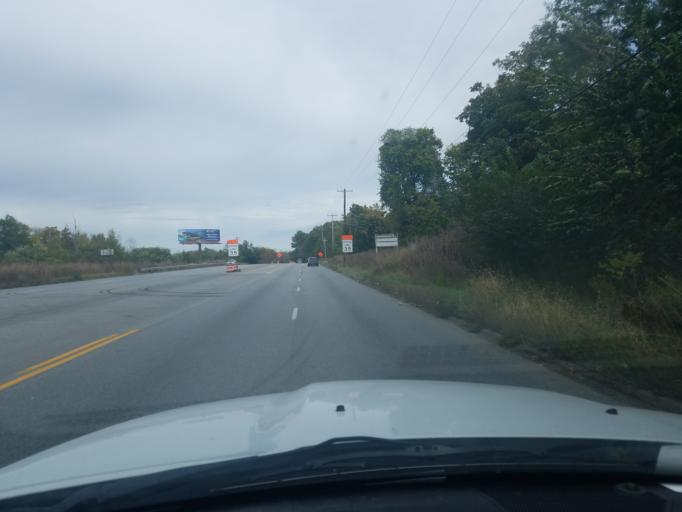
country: US
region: Kentucky
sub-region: Henderson County
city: Henderson
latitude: 37.8861
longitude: -87.5598
